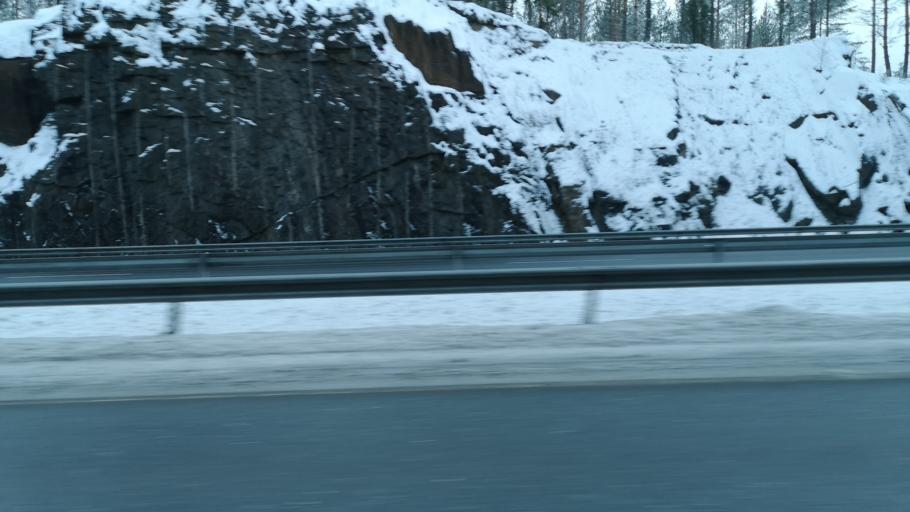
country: FI
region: Uusimaa
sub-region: Helsinki
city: Saukkola
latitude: 60.3207
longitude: 23.9644
